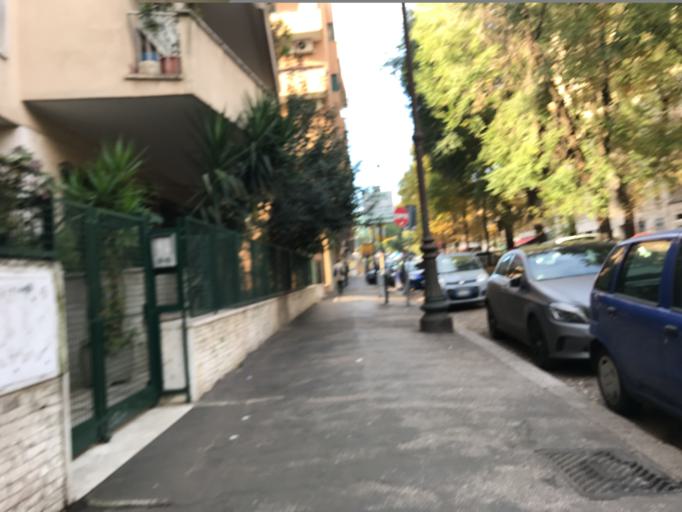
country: IT
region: Latium
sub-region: Citta metropolitana di Roma Capitale
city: Rome
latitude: 41.9071
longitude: 12.5176
